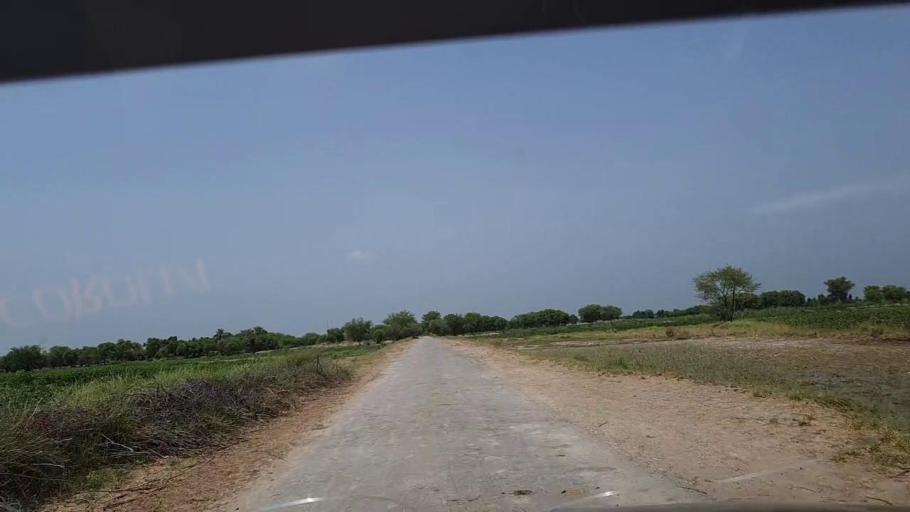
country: PK
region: Sindh
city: Khanpur
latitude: 27.7938
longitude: 69.4550
